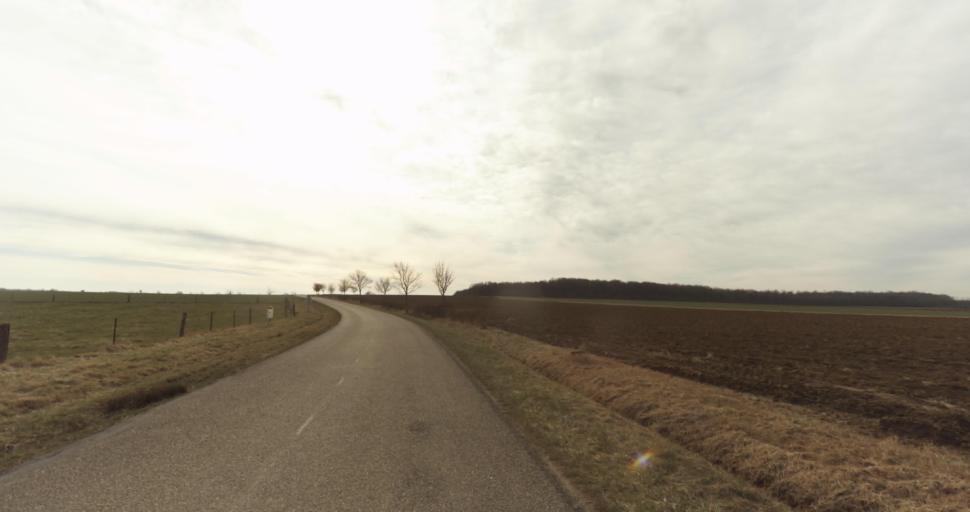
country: FR
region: Lorraine
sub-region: Departement de Meurthe-et-Moselle
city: Conflans-en-Jarnisy
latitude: 49.1402
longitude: 5.8494
